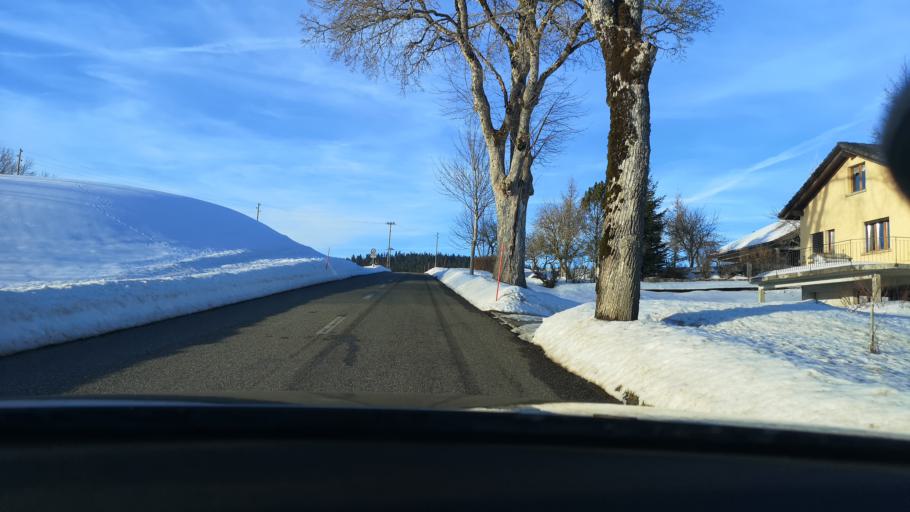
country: CH
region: Neuchatel
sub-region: Val-de-Travers District
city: Fleurier
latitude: 46.9192
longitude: 6.5259
